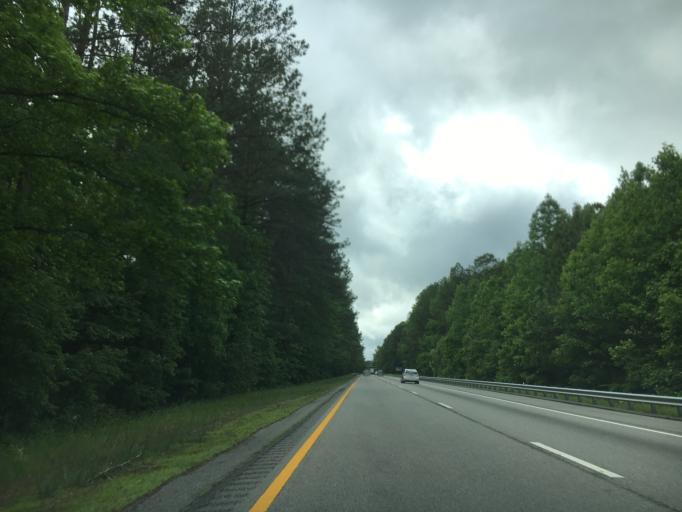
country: US
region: Virginia
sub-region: Mecklenburg County
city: South Hill
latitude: 36.7657
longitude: -78.0712
